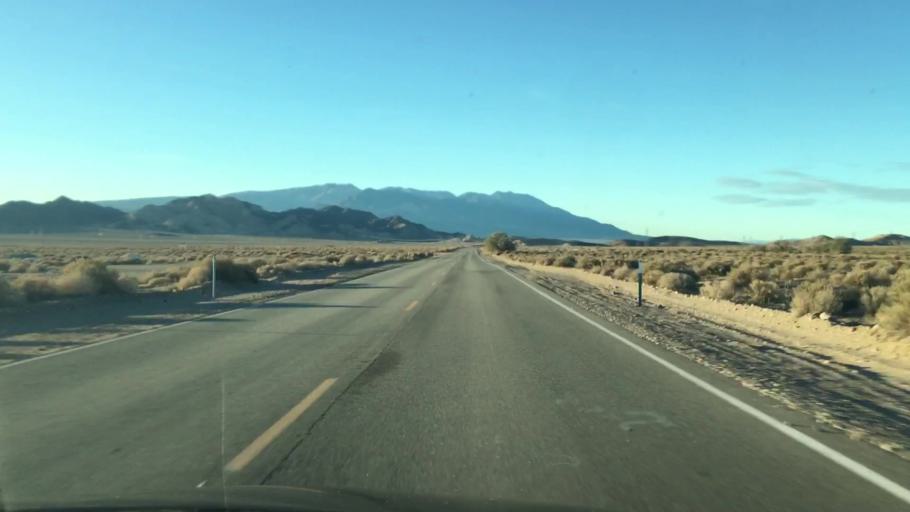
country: US
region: California
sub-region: San Bernardino County
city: Fort Irwin
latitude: 35.3690
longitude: -116.1135
